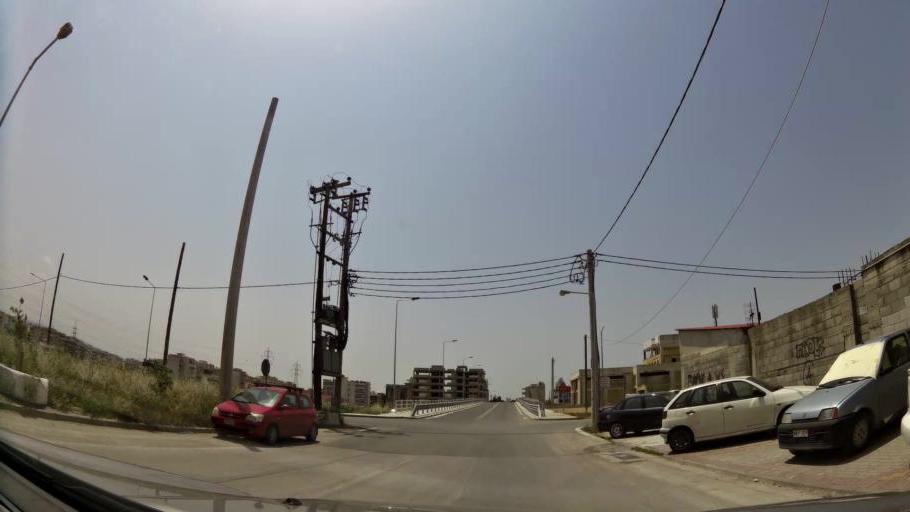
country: GR
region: Central Macedonia
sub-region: Nomos Thessalonikis
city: Evosmos
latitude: 40.6788
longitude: 22.8983
